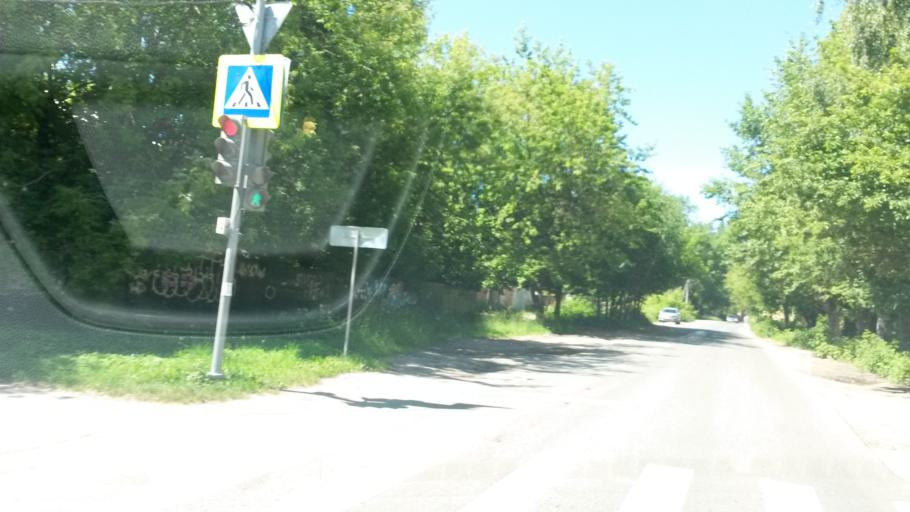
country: RU
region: Ivanovo
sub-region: Gorod Ivanovo
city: Ivanovo
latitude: 56.9805
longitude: 40.9671
